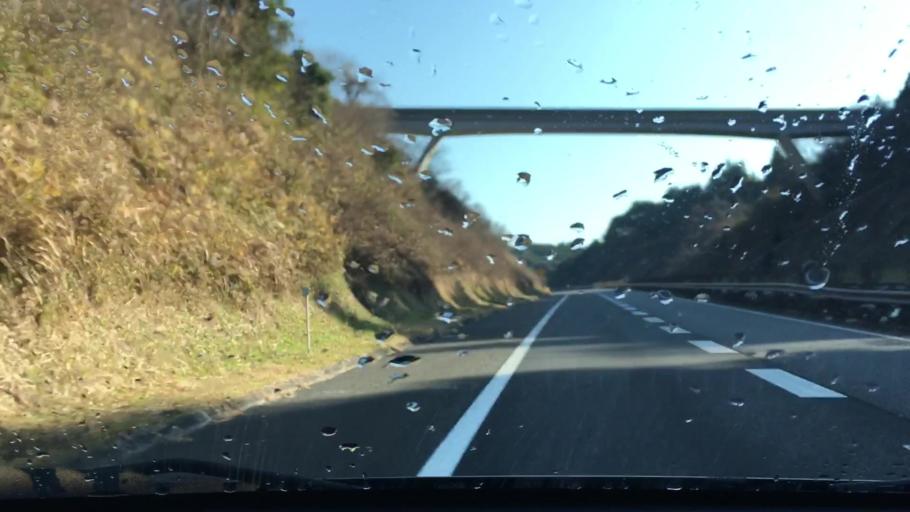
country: JP
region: Kagoshima
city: Kokubu-matsuki
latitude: 31.7433
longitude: 130.8015
